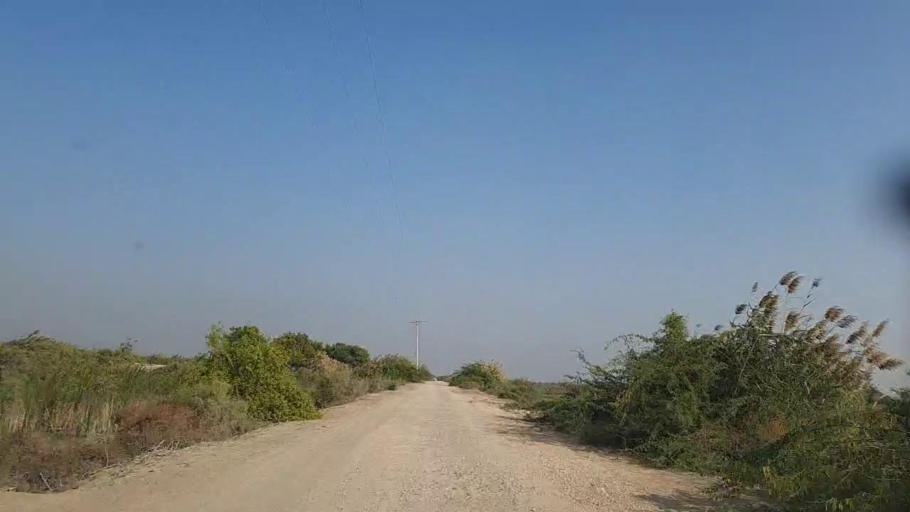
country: PK
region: Sindh
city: Jati
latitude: 24.4602
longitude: 68.3078
